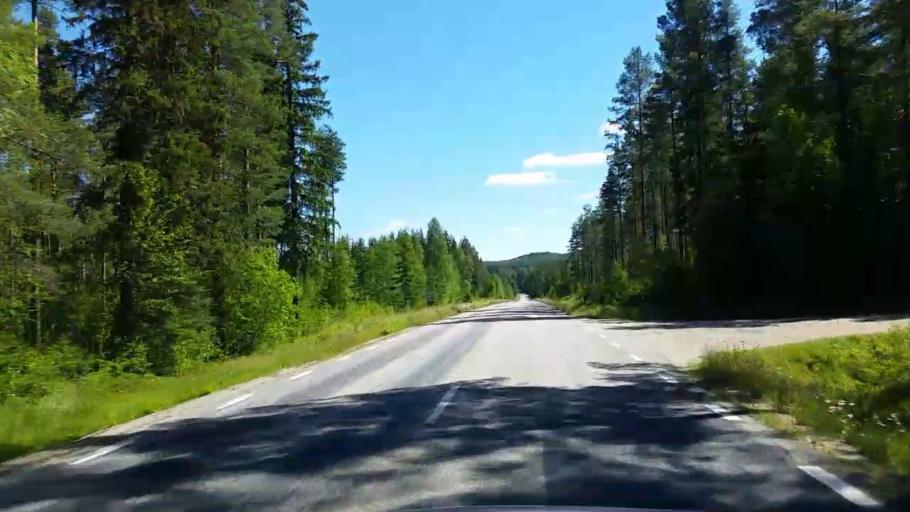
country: SE
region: Gaevleborg
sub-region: Ovanakers Kommun
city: Edsbyn
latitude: 61.3377
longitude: 15.8256
